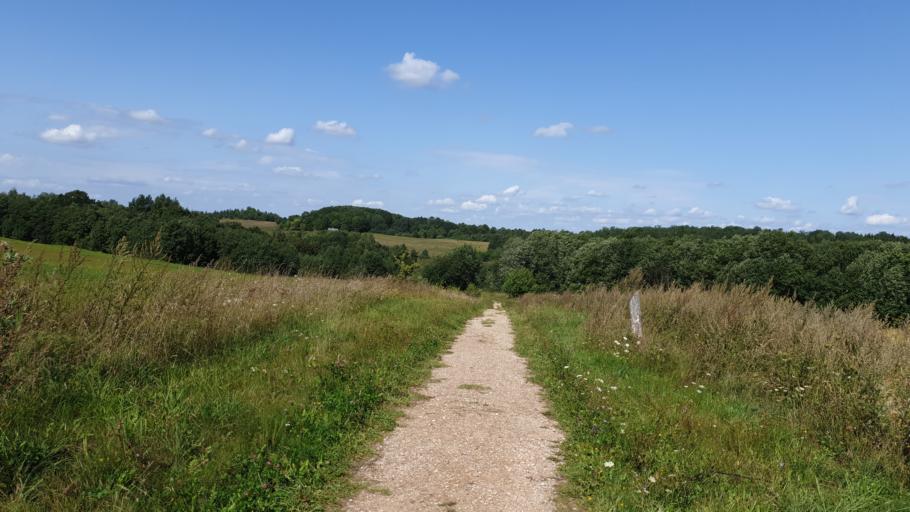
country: LT
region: Vilnius County
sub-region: Vilniaus Rajonas
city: Vievis
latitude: 54.8217
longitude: 24.9459
